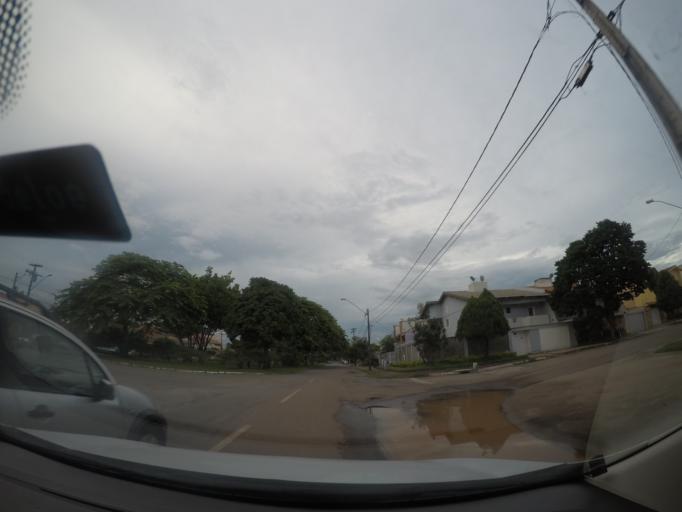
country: BR
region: Goias
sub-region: Goiania
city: Goiania
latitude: -16.6510
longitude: -49.2324
